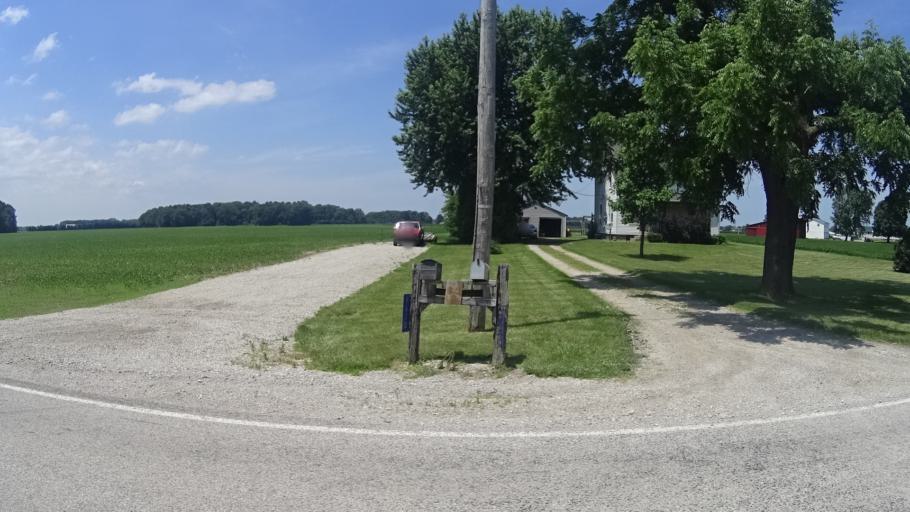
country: US
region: Ohio
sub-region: Erie County
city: Huron
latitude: 41.3498
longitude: -82.5170
